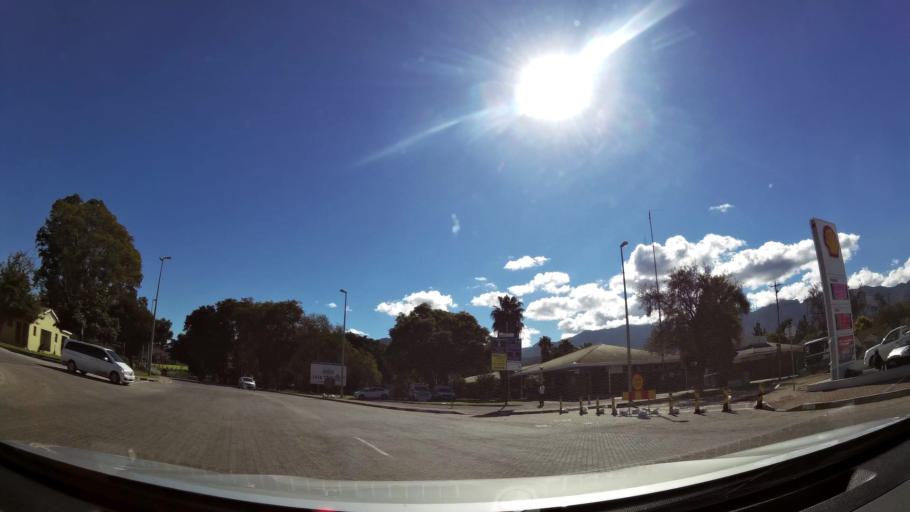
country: ZA
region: Western Cape
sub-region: Cape Winelands District Municipality
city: Ashton
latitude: -33.8057
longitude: 19.8755
